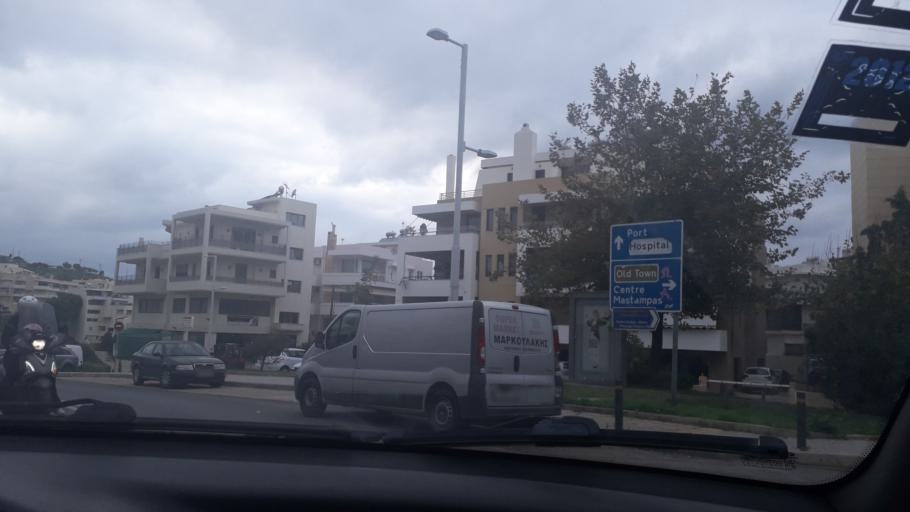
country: GR
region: Crete
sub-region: Nomos Rethymnis
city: Rethymno
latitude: 35.3597
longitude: 24.4764
